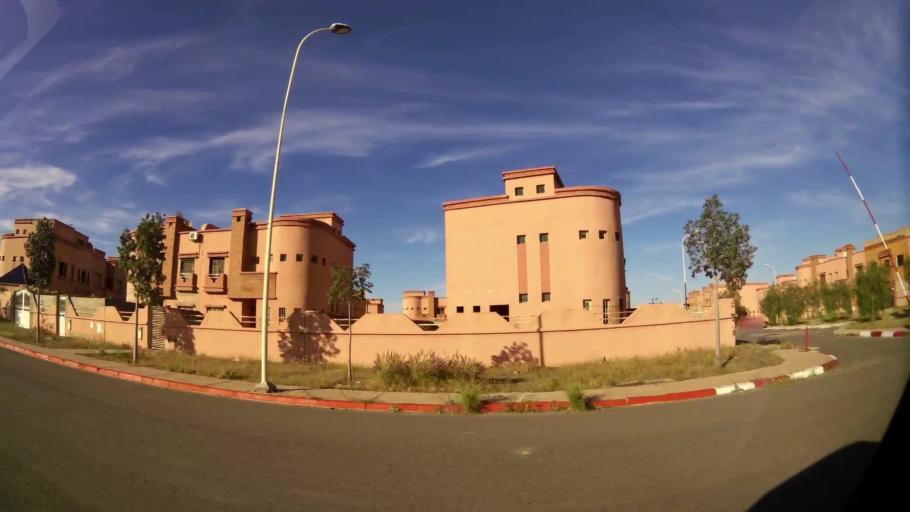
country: MA
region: Marrakech-Tensift-Al Haouz
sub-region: Marrakech
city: Marrakesh
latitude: 31.7573
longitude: -8.1059
